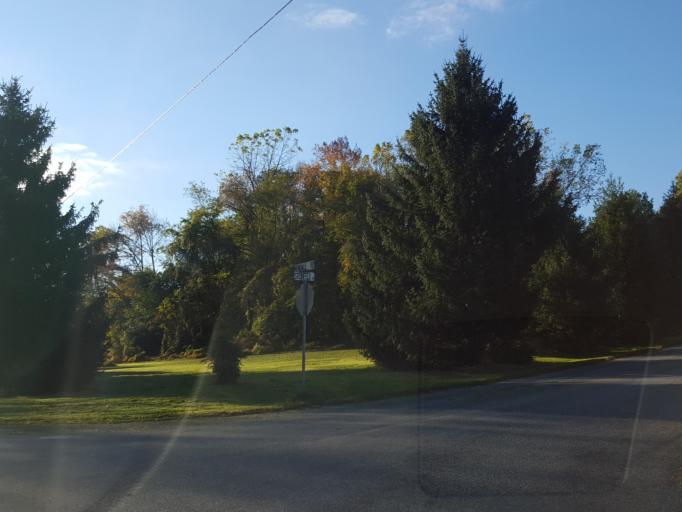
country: US
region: Pennsylvania
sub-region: York County
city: Yoe
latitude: 39.9416
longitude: -76.6320
